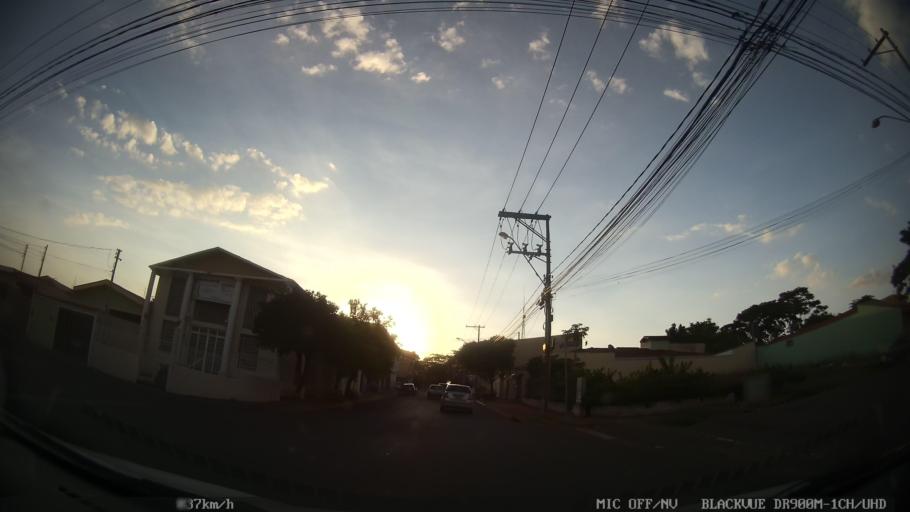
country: BR
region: Sao Paulo
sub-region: Ribeirao Preto
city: Ribeirao Preto
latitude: -21.1590
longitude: -47.8357
